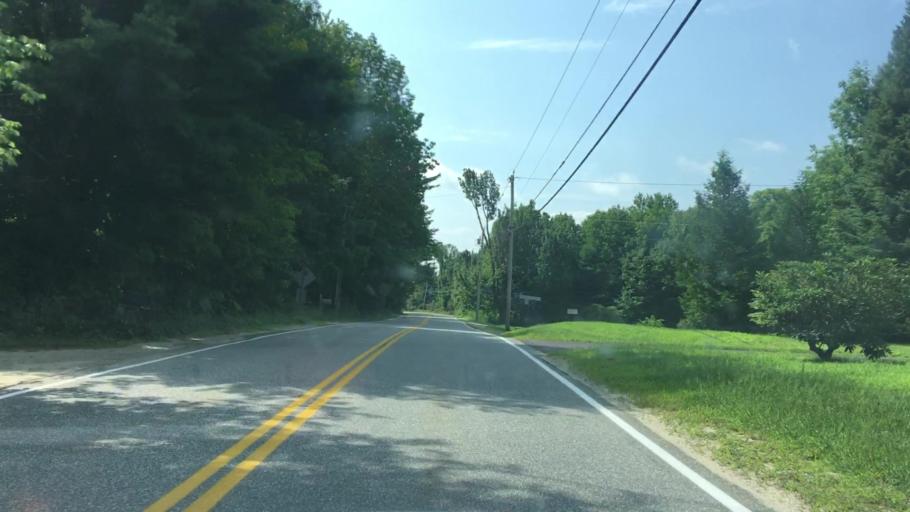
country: US
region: Maine
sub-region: Cumberland County
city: Raymond
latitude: 43.9447
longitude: -70.4387
